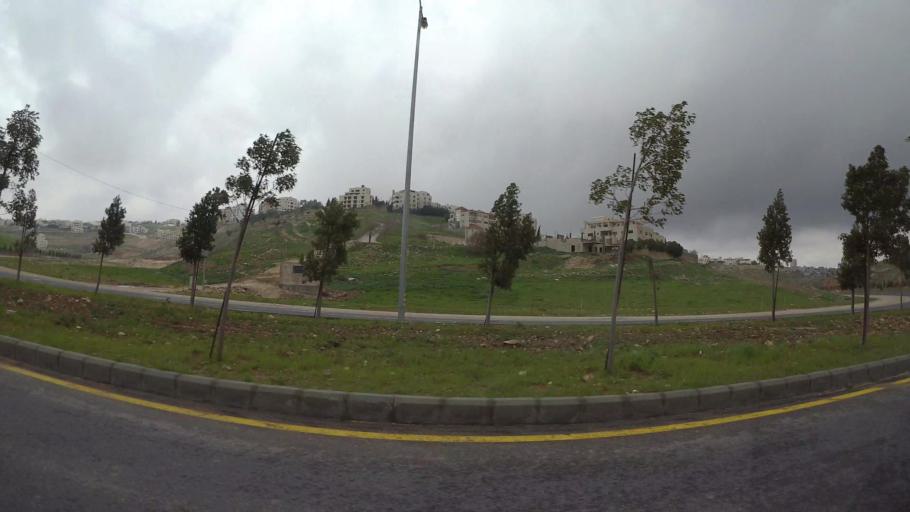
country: JO
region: Amman
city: Al Bunayyat ash Shamaliyah
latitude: 31.9304
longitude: 35.8935
